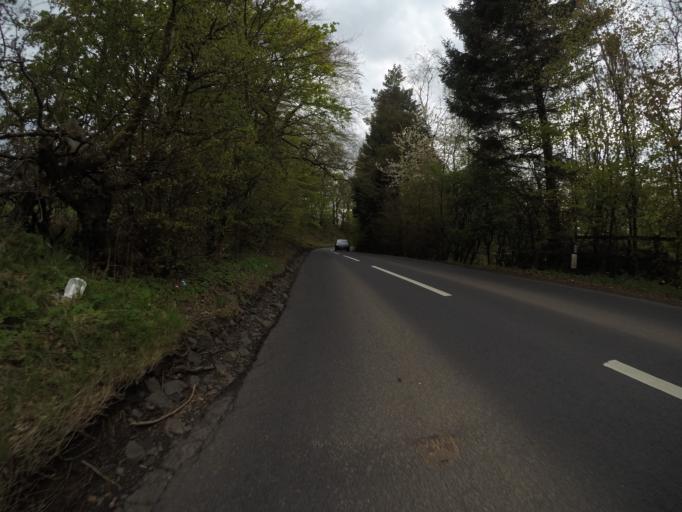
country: GB
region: Scotland
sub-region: East Ayrshire
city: Kilmarnock
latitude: 55.6457
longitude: -4.4927
